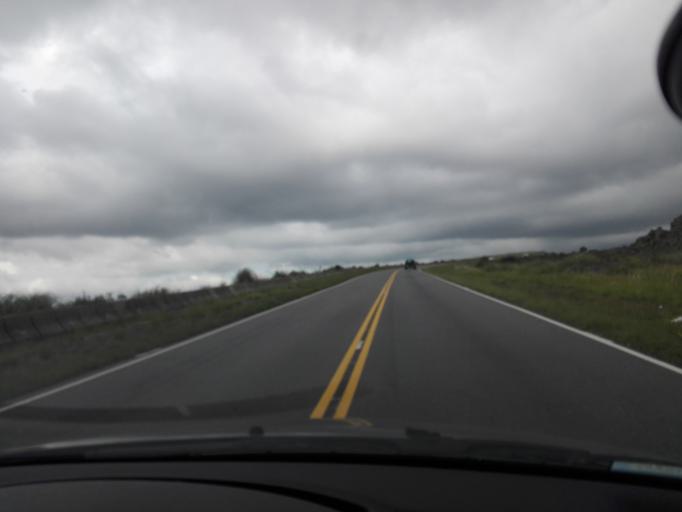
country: AR
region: Cordoba
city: Cuesta Blanca
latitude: -31.6028
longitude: -64.6747
